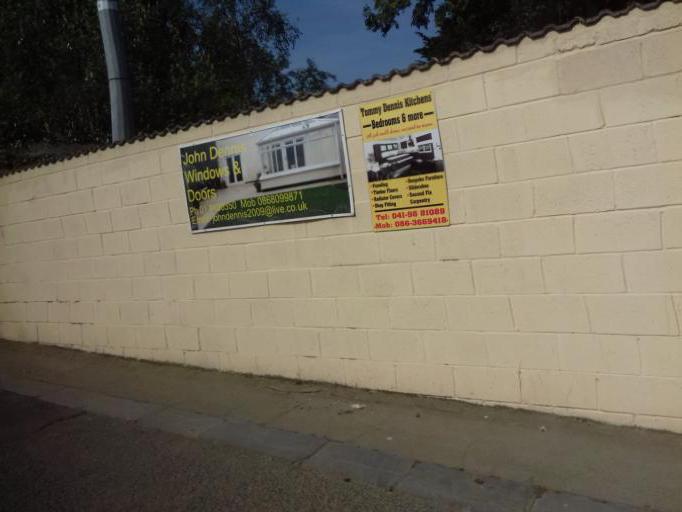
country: IE
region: Leinster
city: Lusk
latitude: 53.5283
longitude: -6.1700
